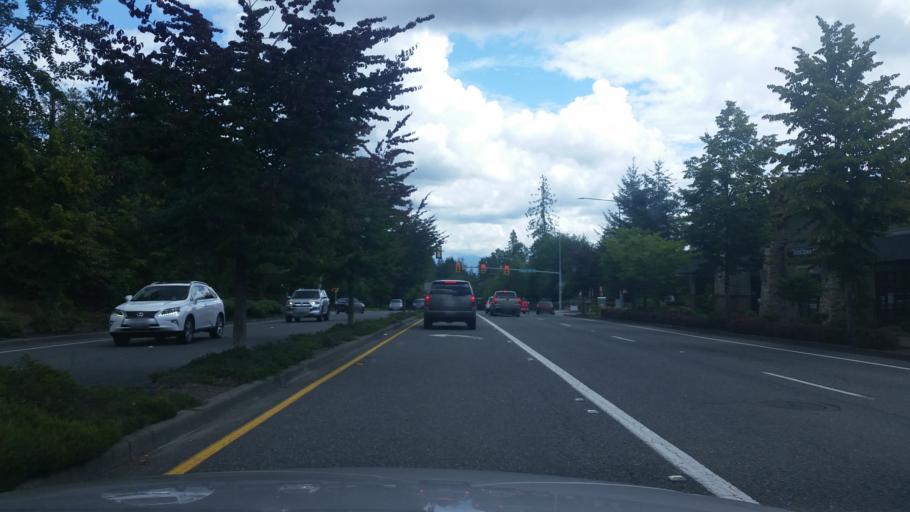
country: US
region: Washington
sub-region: King County
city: Union Hill-Novelty Hill
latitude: 47.7002
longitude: -122.0253
